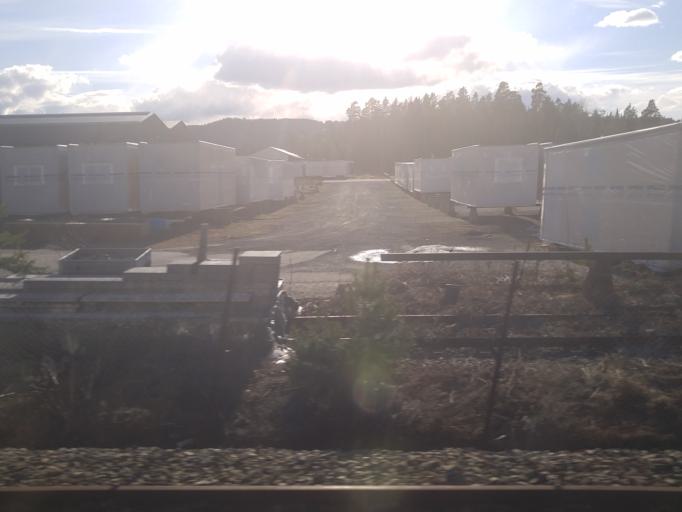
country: NO
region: Hedmark
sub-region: Ringsaker
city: Moelv
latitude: 60.9354
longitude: 10.6934
